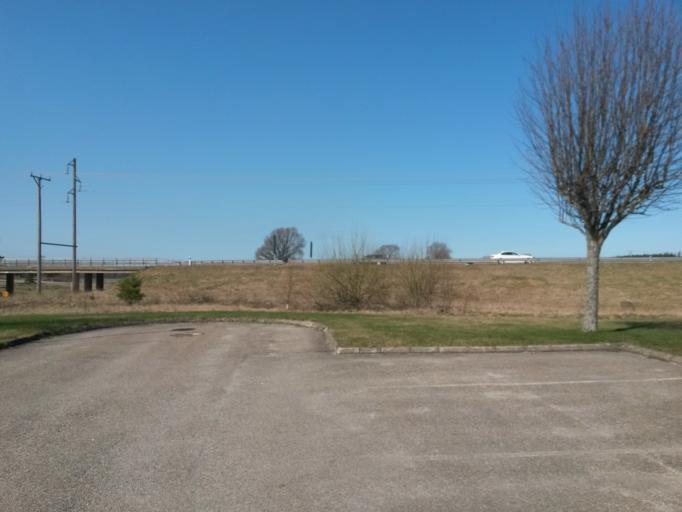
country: SE
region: Vaestra Goetaland
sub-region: Vargarda Kommun
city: Vargarda
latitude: 58.0422
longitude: 12.8001
